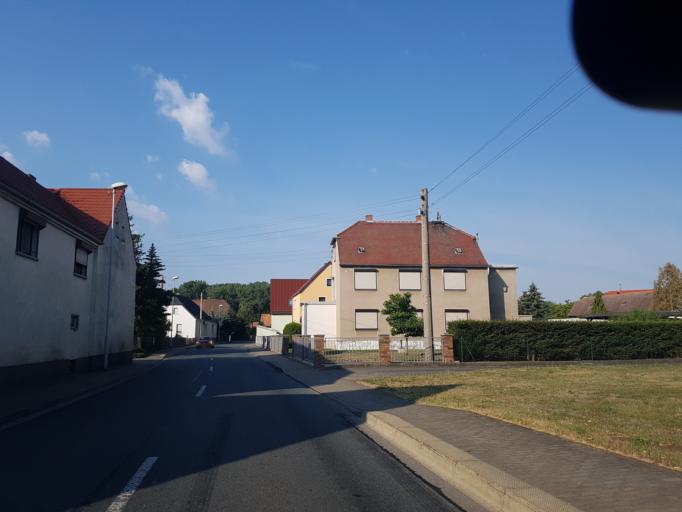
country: DE
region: Saxony
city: Stauchitz
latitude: 51.2580
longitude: 13.2439
